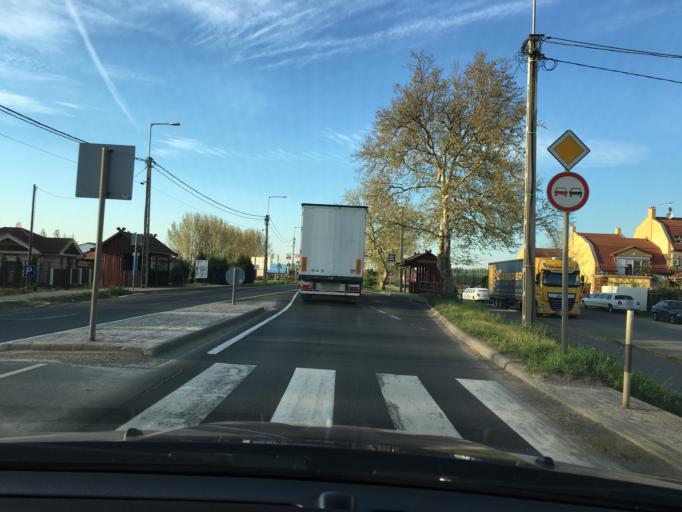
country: HU
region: Hajdu-Bihar
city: Mikepercs
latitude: 47.4493
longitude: 21.6327
